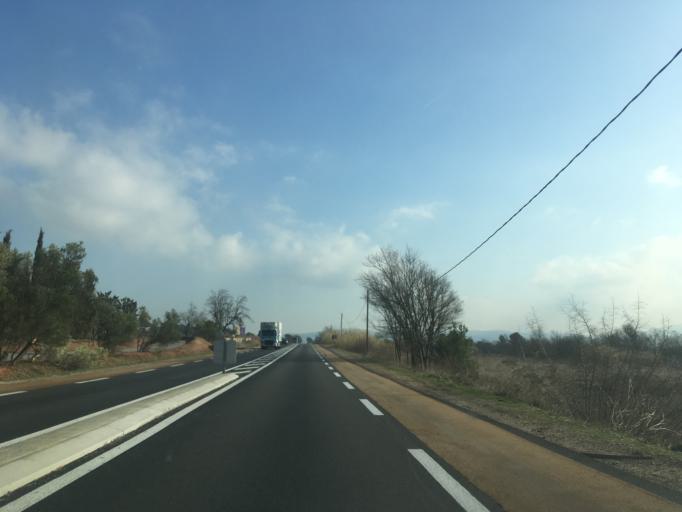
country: FR
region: Provence-Alpes-Cote d'Azur
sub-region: Departement du Var
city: Vidauban
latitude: 43.4037
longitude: 6.3943
